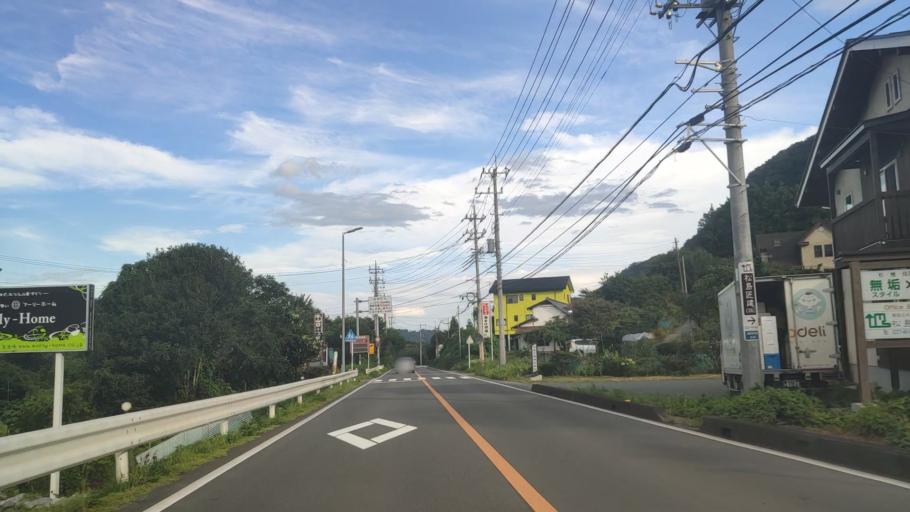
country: JP
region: Gunma
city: Omamacho-omama
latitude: 36.4601
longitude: 139.2622
